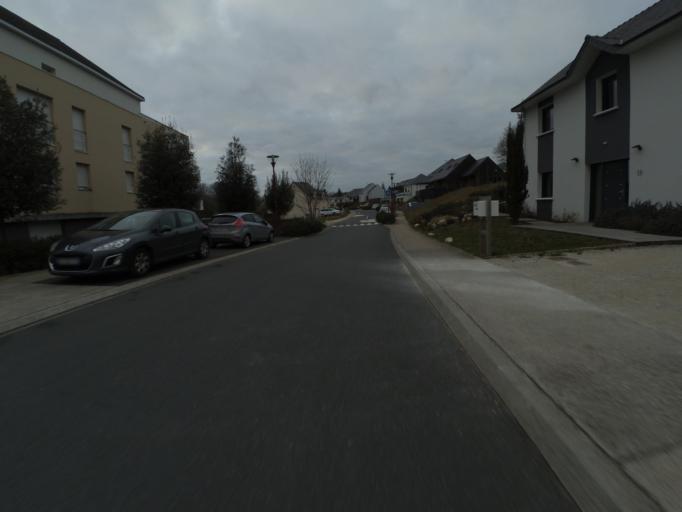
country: FR
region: Pays de la Loire
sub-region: Departement de la Loire-Atlantique
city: Carquefou
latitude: 47.3070
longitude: -1.4850
